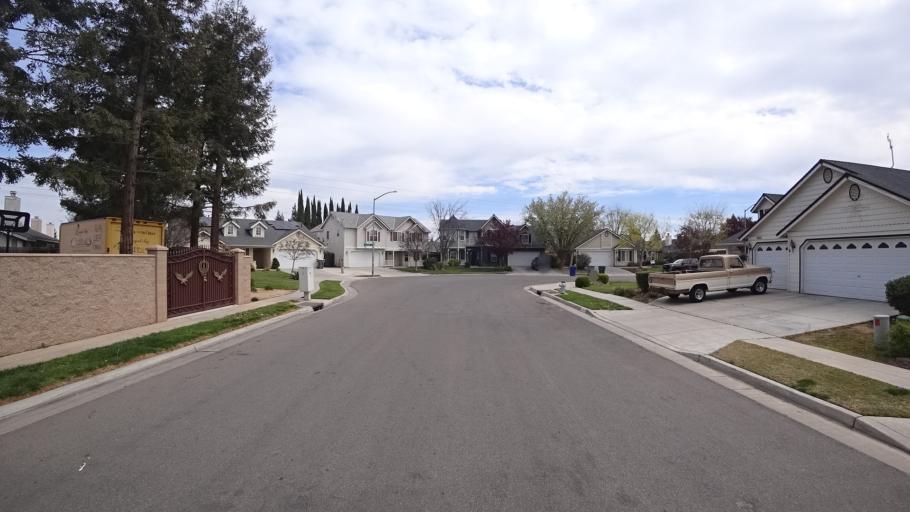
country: US
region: California
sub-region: Fresno County
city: Biola
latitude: 36.8317
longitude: -119.8950
